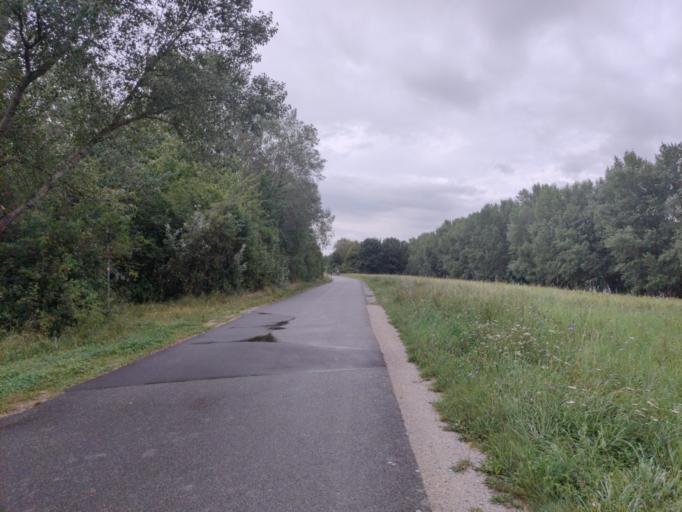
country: AT
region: Lower Austria
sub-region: Politischer Bezirk Korneuburg
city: Langenzersdorf
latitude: 48.2848
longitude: 16.3555
